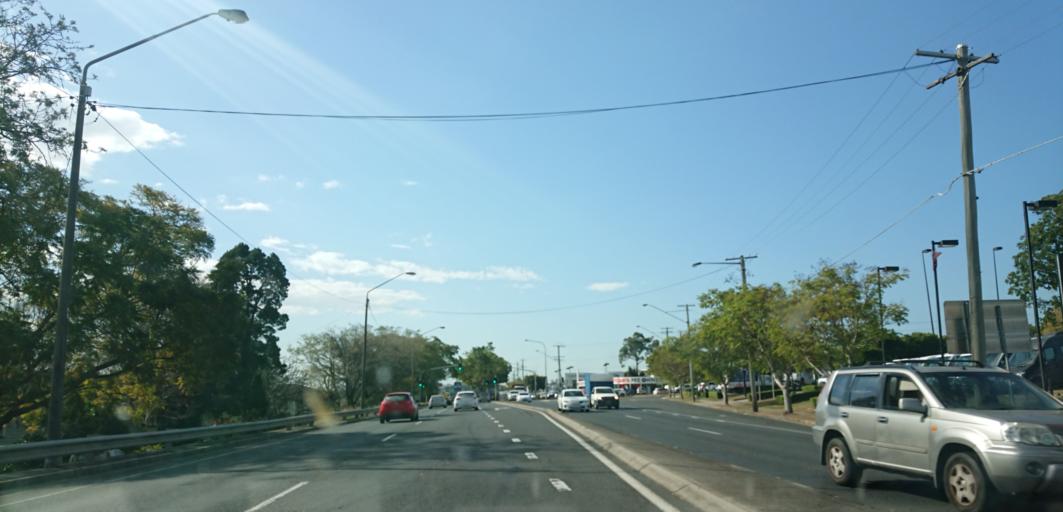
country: AU
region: Queensland
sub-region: Brisbane
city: Rocklea
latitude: -27.5392
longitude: 153.0135
